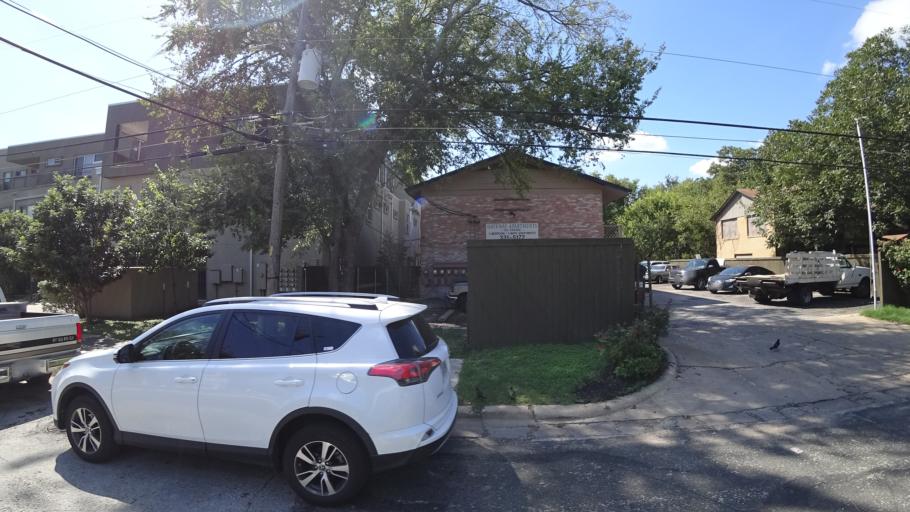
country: US
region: Texas
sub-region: Travis County
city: Austin
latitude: 30.3353
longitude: -97.7151
